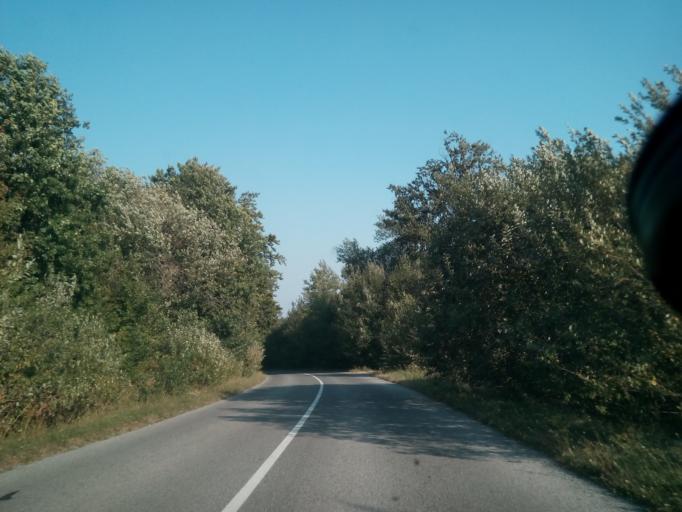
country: SK
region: Kosicky
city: Kosice
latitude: 48.7252
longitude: 21.1266
